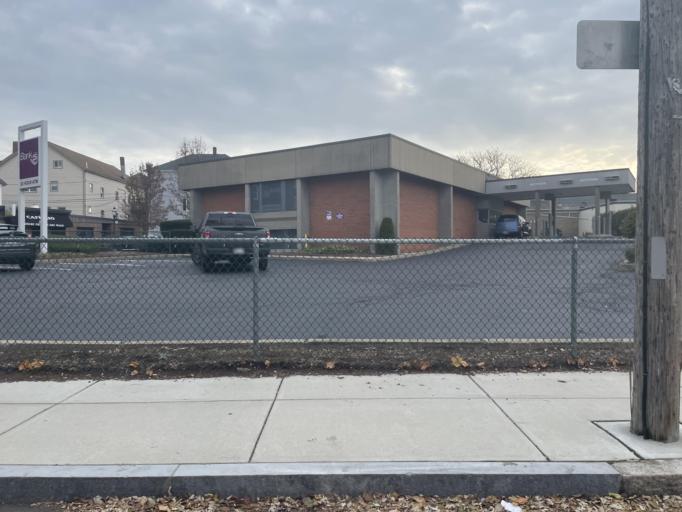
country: US
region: Massachusetts
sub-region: Bristol County
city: Fall River
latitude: 41.6918
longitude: -71.1361
